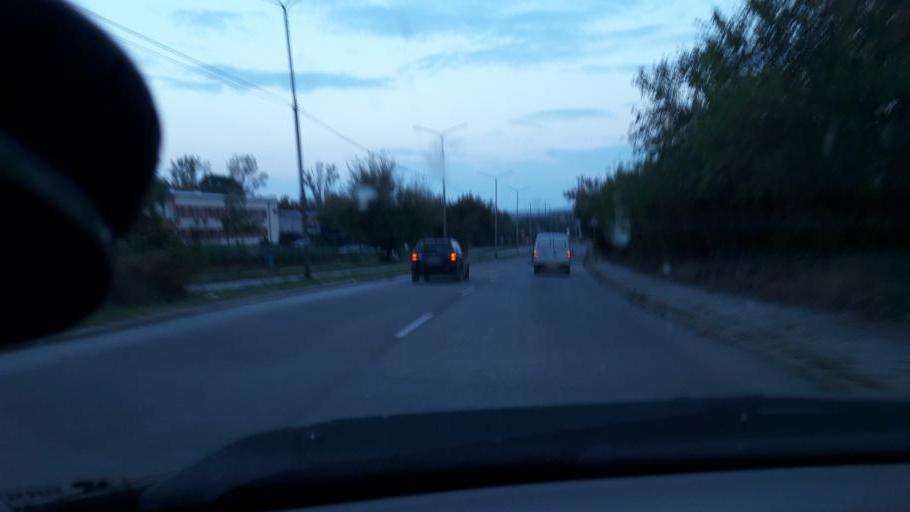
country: BG
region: Razgrad
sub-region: Obshtina Razgrad
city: Razgrad
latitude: 43.5389
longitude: 26.5178
